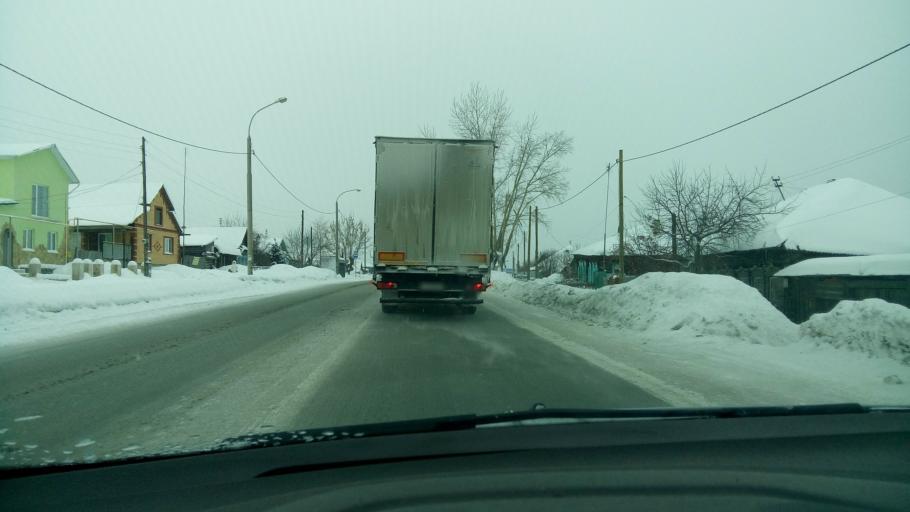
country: RU
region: Sverdlovsk
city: Beloyarskiy
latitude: 56.7567
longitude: 61.3964
